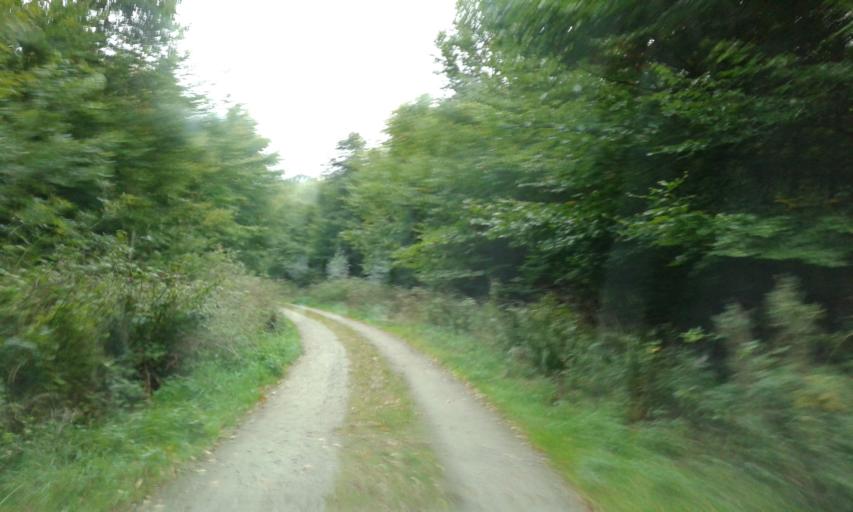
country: PL
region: West Pomeranian Voivodeship
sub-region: Powiat choszczenski
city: Pelczyce
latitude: 53.0888
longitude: 15.2488
